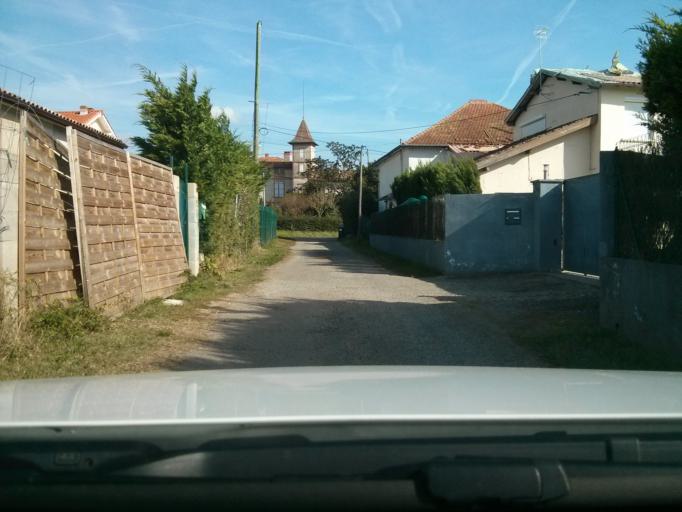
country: FR
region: Midi-Pyrenees
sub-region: Departement du Tarn-et-Garonne
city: Montauban
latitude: 44.0095
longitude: 1.3256
